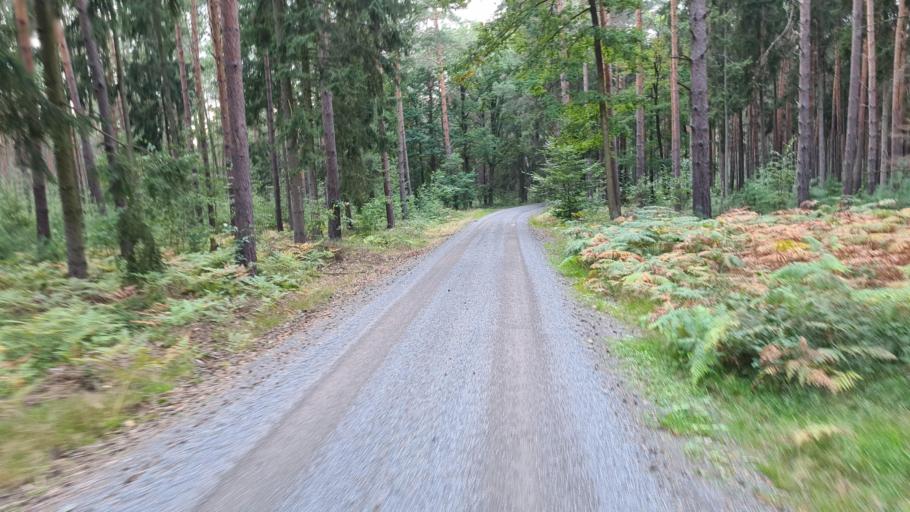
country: DE
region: Brandenburg
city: Schonborn
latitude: 51.6202
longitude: 13.4747
